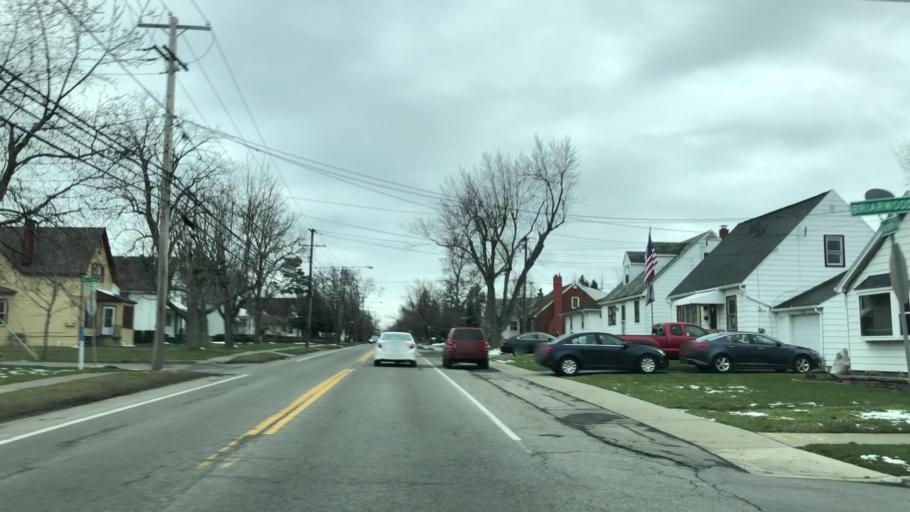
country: US
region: New York
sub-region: Erie County
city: Lancaster
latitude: 42.8891
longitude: -78.6767
